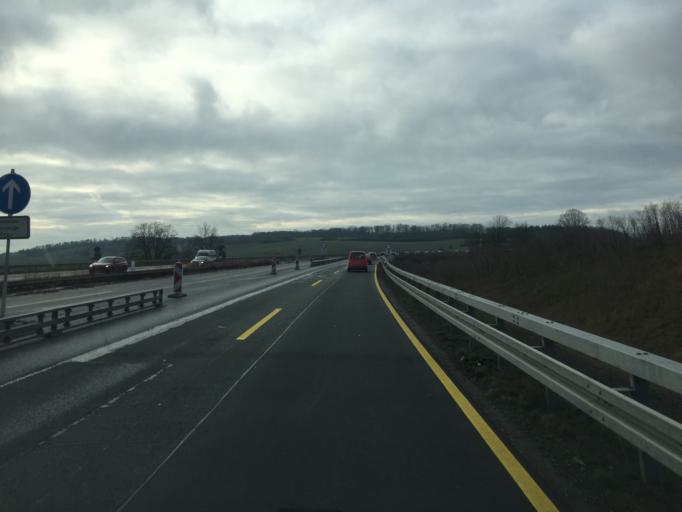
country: DE
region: Lower Saxony
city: Northeim
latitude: 51.7419
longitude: 10.0042
